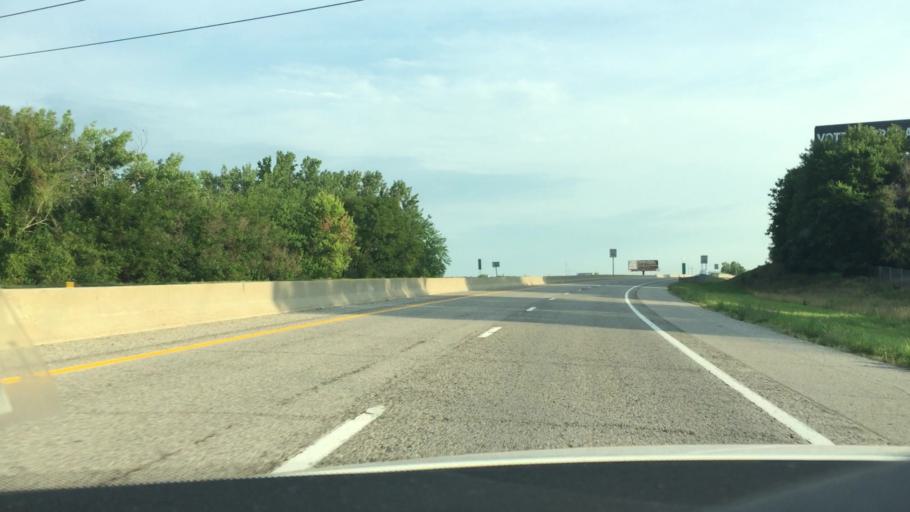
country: US
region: Kansas
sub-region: Doniphan County
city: Elwood
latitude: 39.7356
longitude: -94.8499
